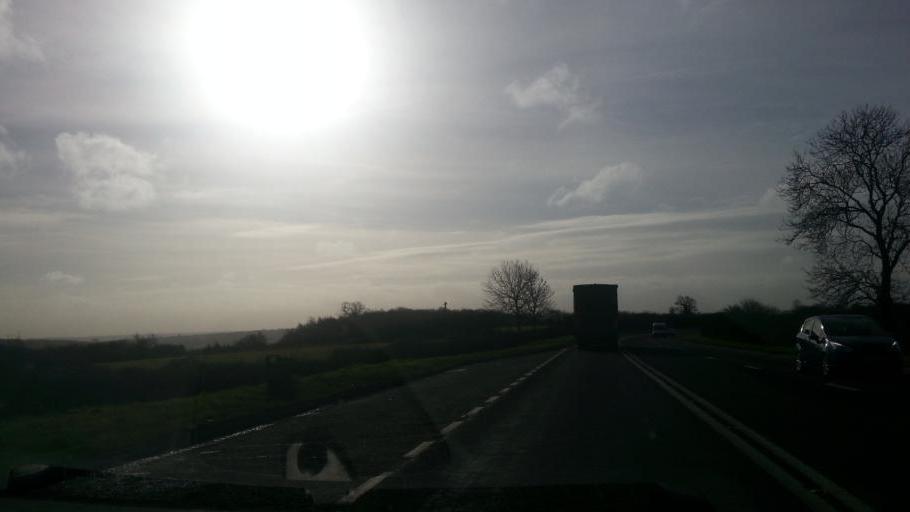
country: GB
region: England
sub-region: District of Rutland
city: Ridlington
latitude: 52.5982
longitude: -0.7577
